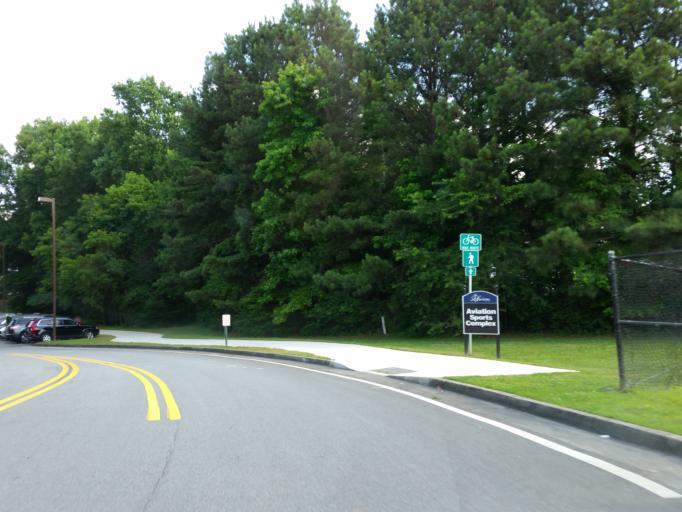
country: US
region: Georgia
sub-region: Cobb County
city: Marietta
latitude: 33.9408
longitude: -84.5288
